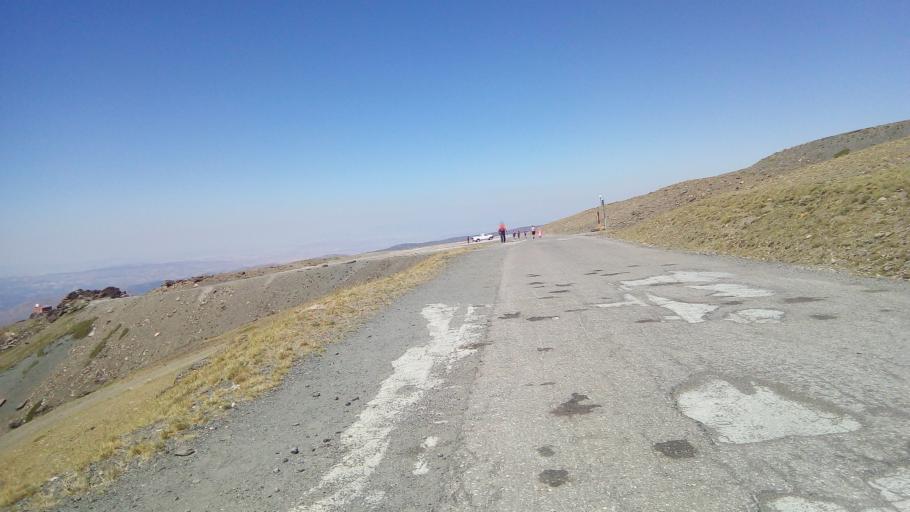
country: ES
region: Andalusia
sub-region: Provincia de Granada
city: Guejar-Sierra
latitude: 37.0833
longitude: -3.3819
